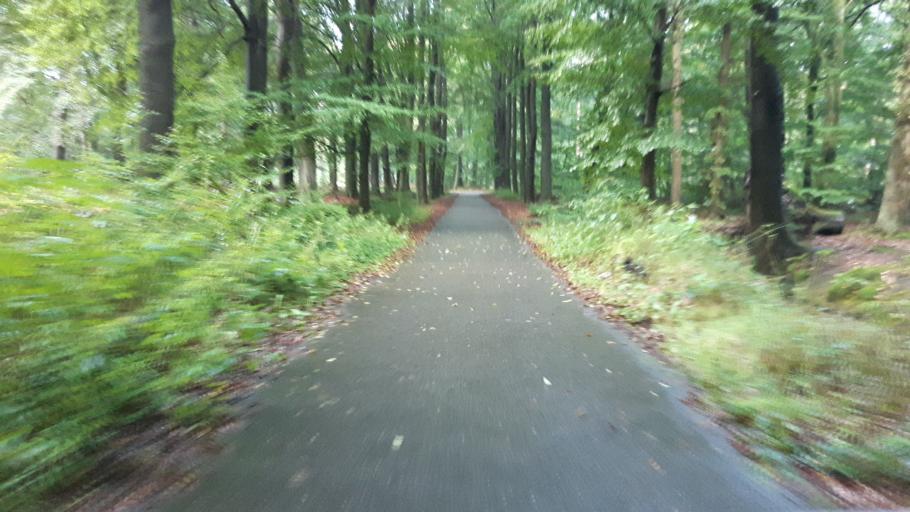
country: NL
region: Friesland
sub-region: Gemeente Smallingerland
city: Drachten
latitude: 53.0636
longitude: 6.1255
